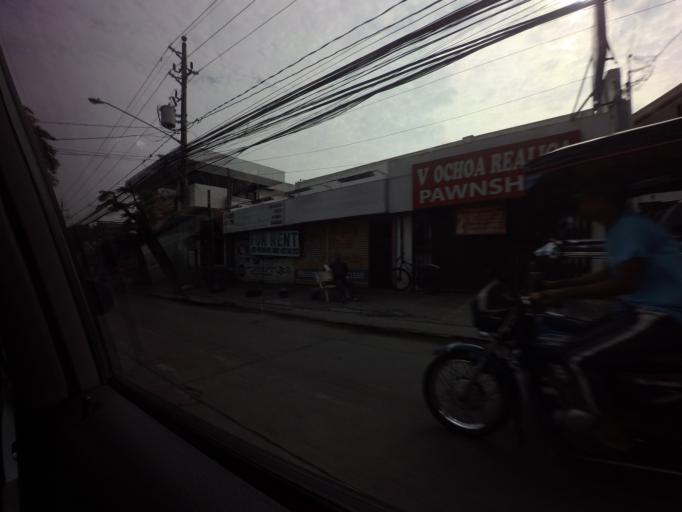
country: PH
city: Sambayanihan People's Village
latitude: 14.4507
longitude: 121.0185
